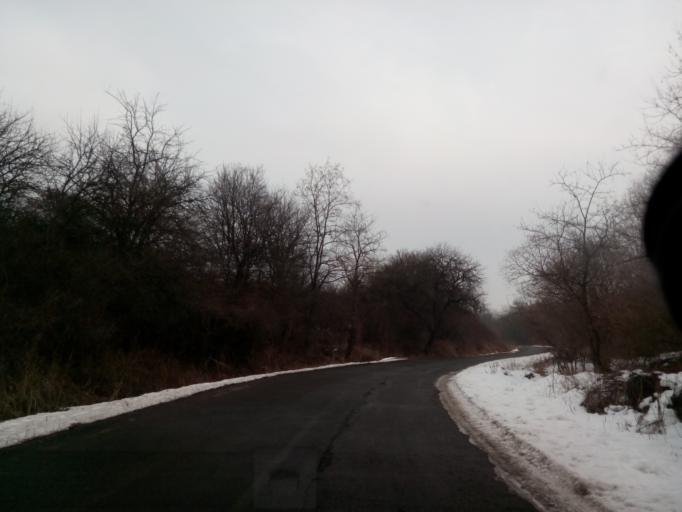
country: HU
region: Borsod-Abauj-Zemplen
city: Gonc
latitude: 48.4861
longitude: 21.3706
